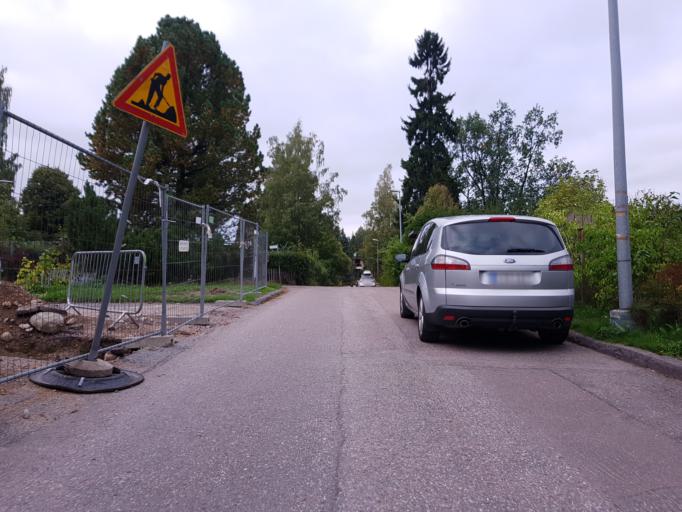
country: FI
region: Uusimaa
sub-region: Helsinki
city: Helsinki
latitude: 60.2278
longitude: 24.9801
